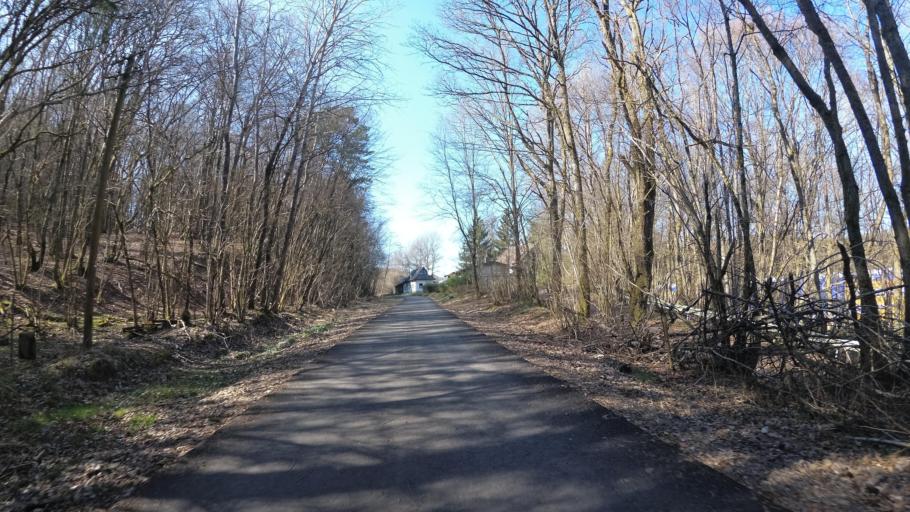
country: DE
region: Rheinland-Pfalz
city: Achtelsbach
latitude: 49.5838
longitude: 7.0753
